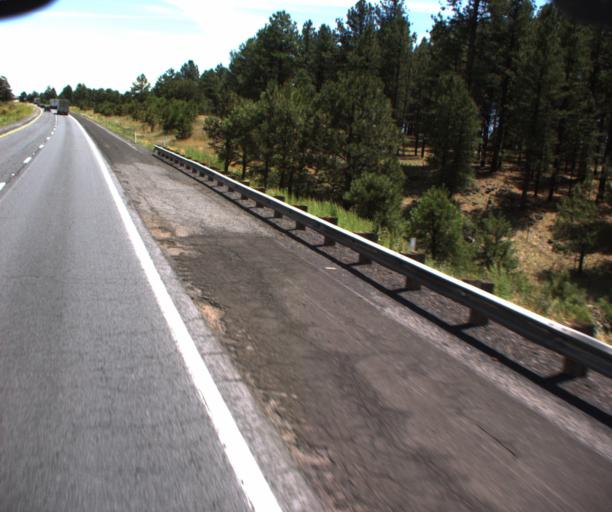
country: US
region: Arizona
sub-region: Coconino County
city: Parks
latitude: 35.2485
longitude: -111.9880
